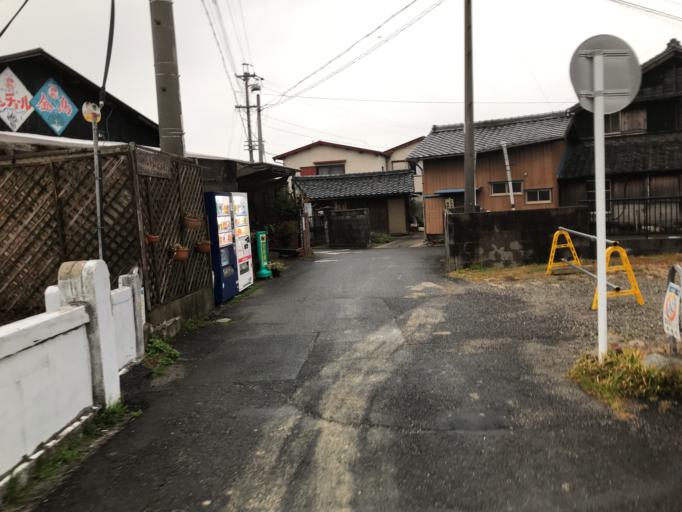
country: JP
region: Aichi
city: Tokoname
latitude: 34.8898
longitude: 136.8404
